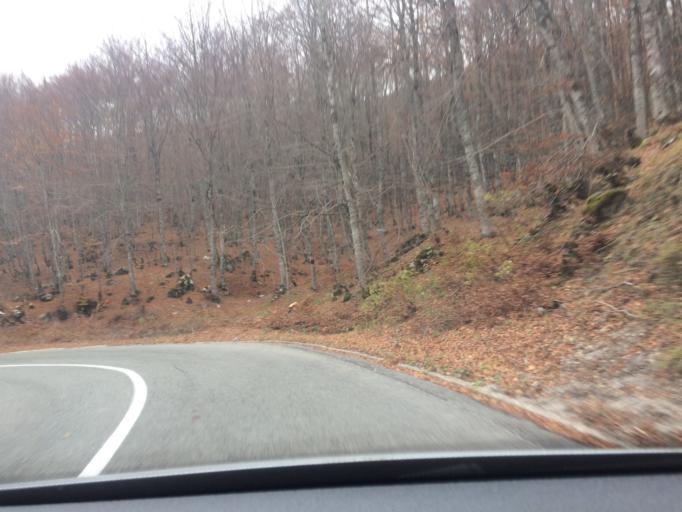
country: ME
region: Opstina Savnik
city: Savnik
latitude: 42.9008
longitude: 19.0910
